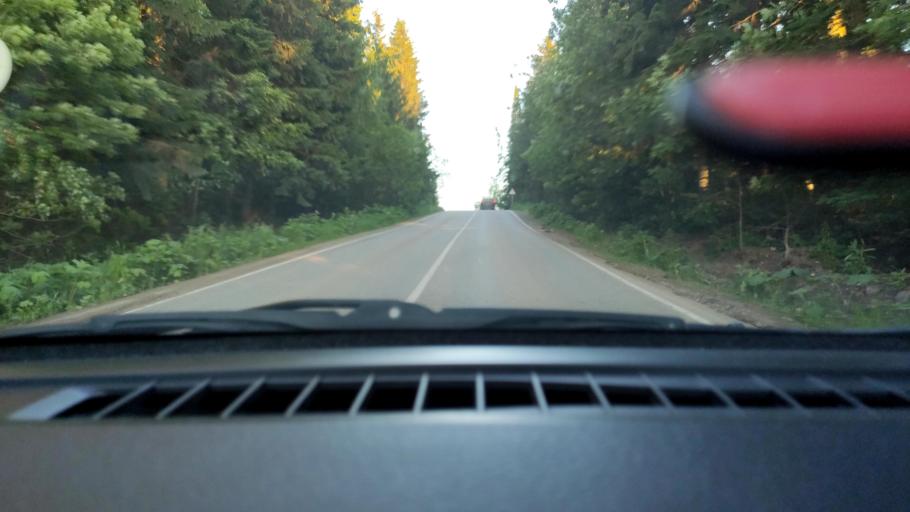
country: RU
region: Perm
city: Kultayevo
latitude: 57.9203
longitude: 55.9277
